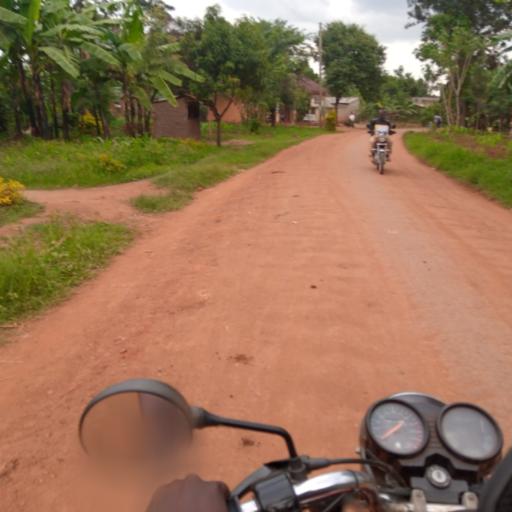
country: UG
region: Eastern Region
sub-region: Mbale District
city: Mbale
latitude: 1.1077
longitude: 34.1789
